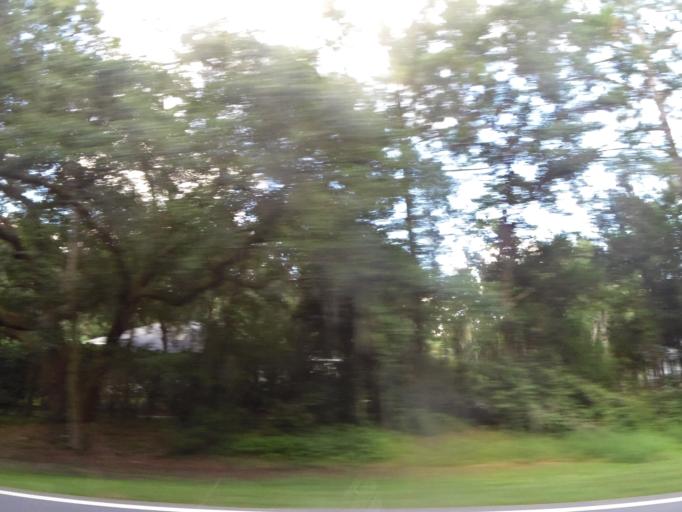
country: US
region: Georgia
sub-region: Glynn County
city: Saint Simon Mills
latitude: 31.1725
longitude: -81.4017
